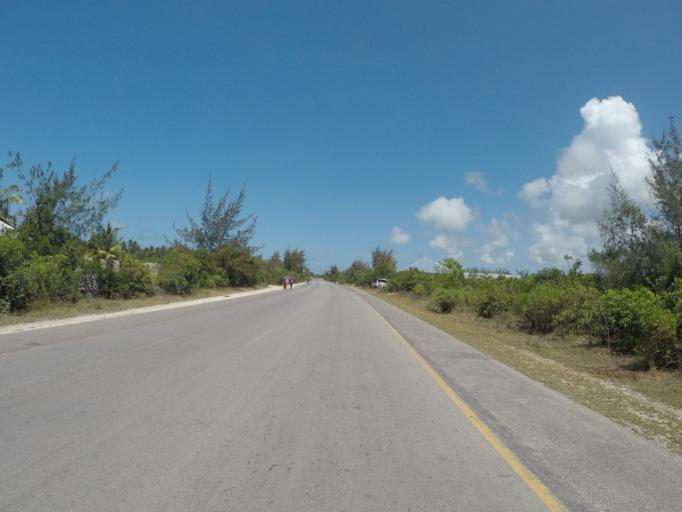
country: TZ
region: Zanzibar Central/South
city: Nganane
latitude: -6.3185
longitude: 39.5429
